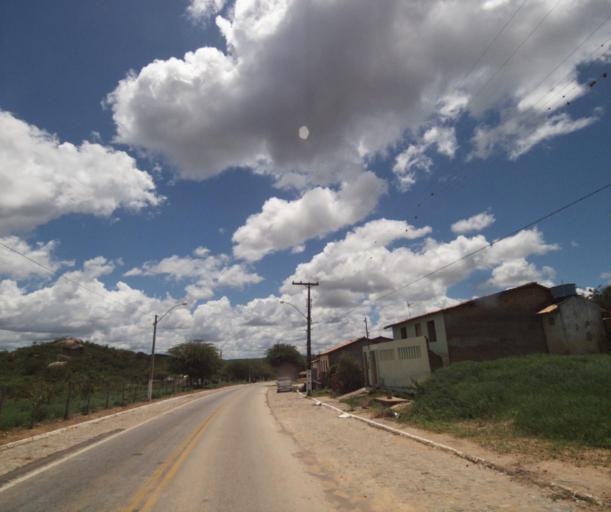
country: BR
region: Bahia
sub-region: Pocoes
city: Pocoes
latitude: -14.3788
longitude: -40.5081
